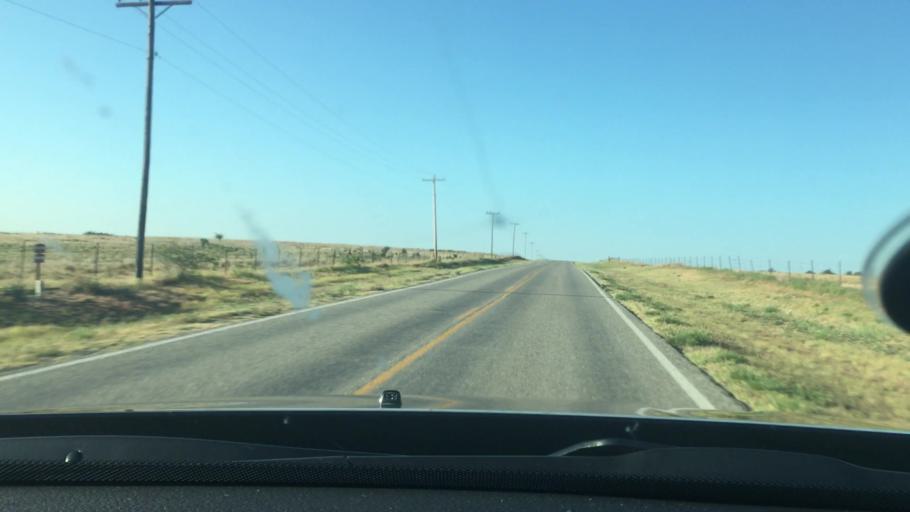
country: US
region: Oklahoma
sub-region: Murray County
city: Sulphur
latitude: 34.5862
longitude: -96.8449
